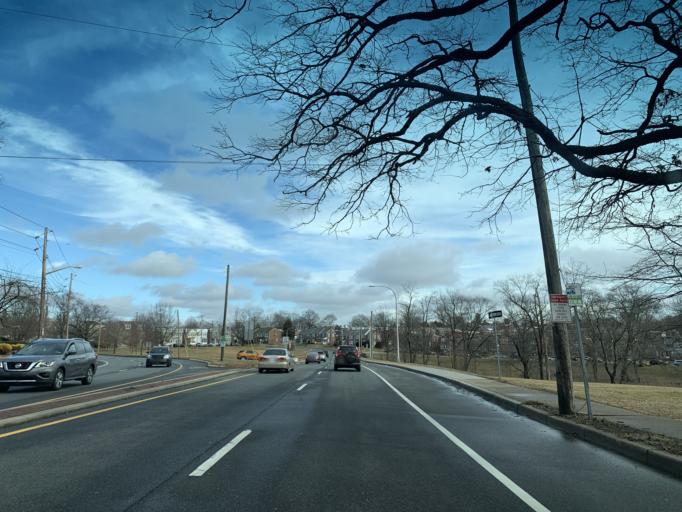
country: US
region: Delaware
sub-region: New Castle County
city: Elsmere
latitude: 39.7419
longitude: -75.5789
